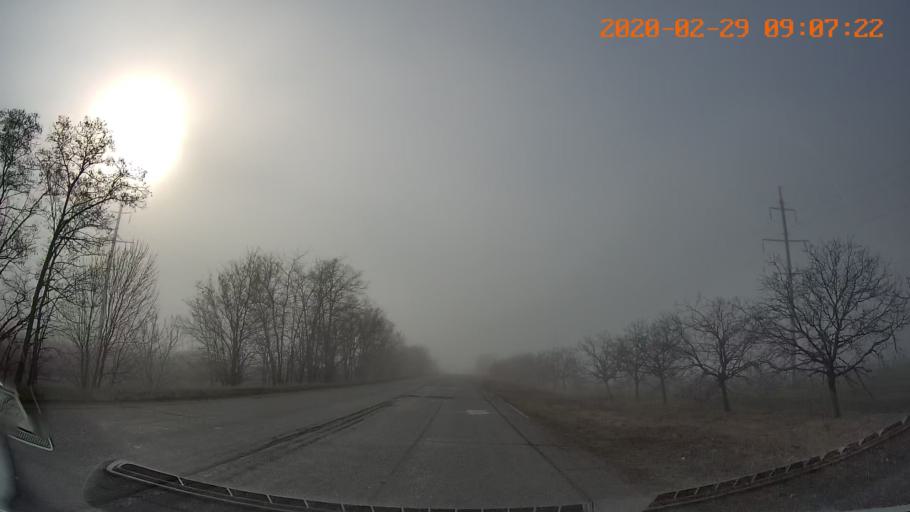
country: MD
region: Telenesti
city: Tiraspolul Nou
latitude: 46.8629
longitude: 29.7486
